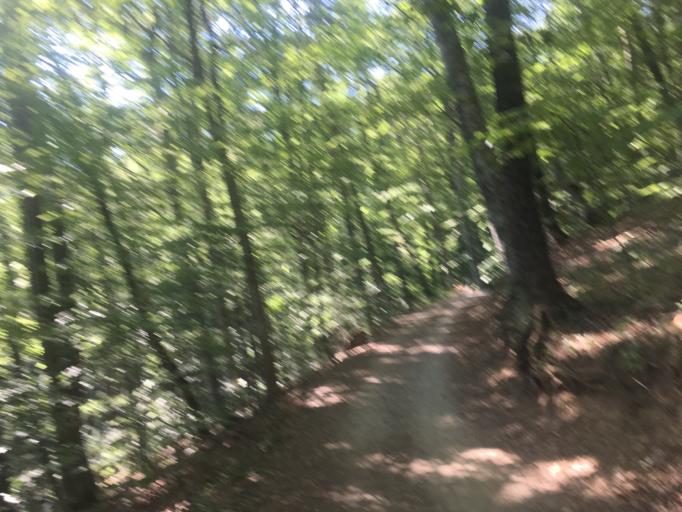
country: XK
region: Pristina
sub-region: Komuna e Prishtines
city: Pristina
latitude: 42.6639
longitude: 21.2196
